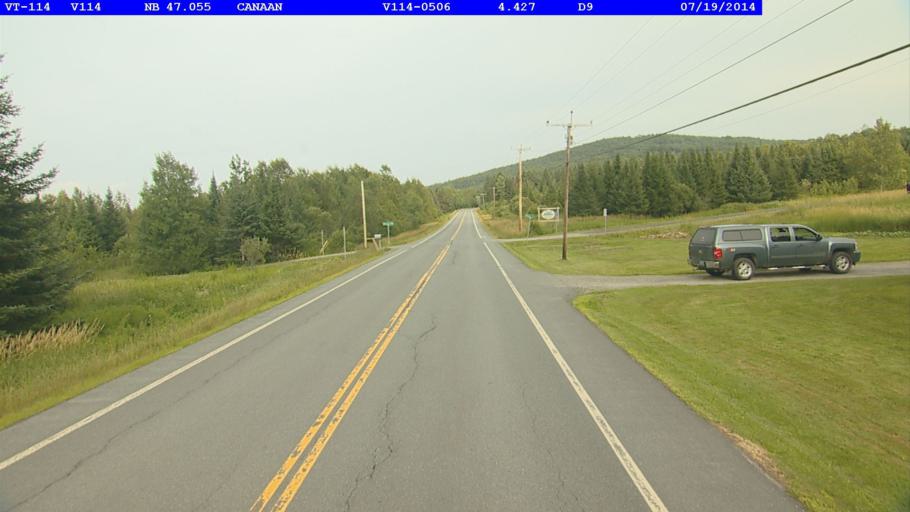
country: US
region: New Hampshire
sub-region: Coos County
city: Colebrook
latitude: 45.0075
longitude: -71.6059
